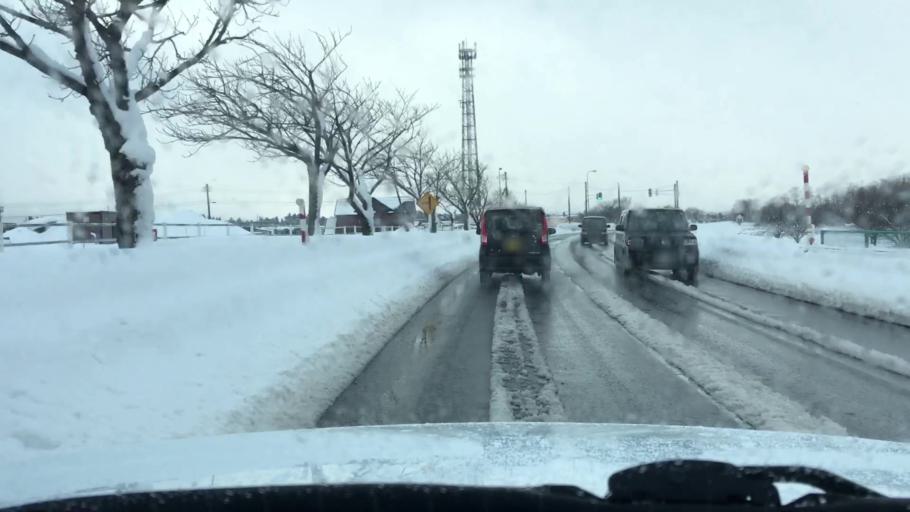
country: JP
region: Aomori
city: Hirosaki
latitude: 40.6227
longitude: 140.4726
